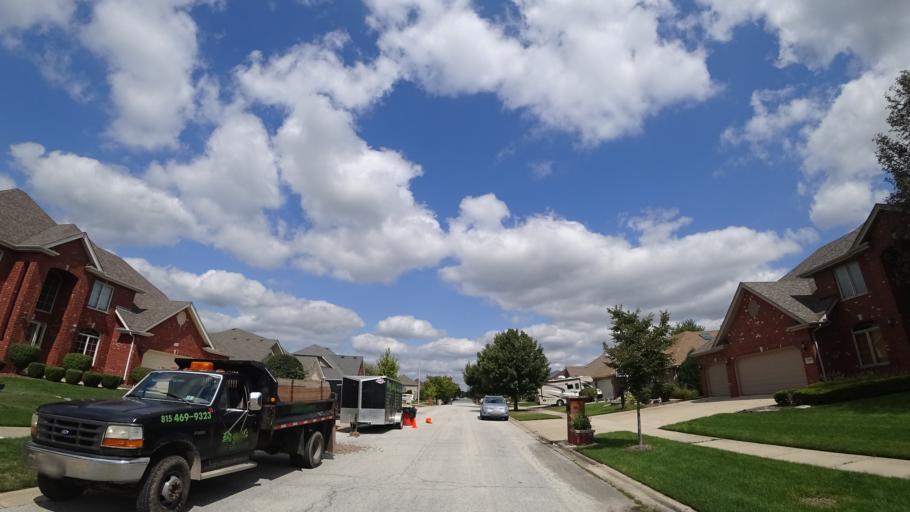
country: US
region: Illinois
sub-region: Cook County
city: Orland Hills
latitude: 41.5696
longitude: -87.8743
